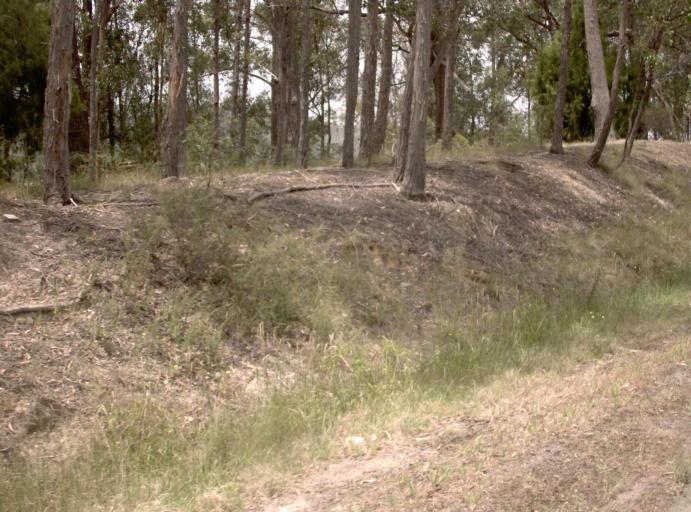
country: AU
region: Victoria
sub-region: Latrobe
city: Traralgon
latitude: -38.4418
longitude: 146.7326
